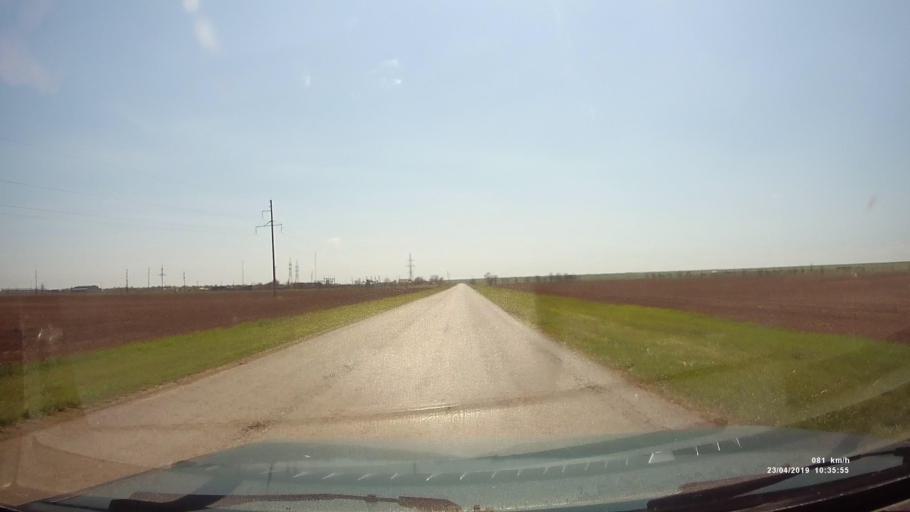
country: RU
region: Kalmykiya
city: Yashalta
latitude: 46.5496
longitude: 42.6299
